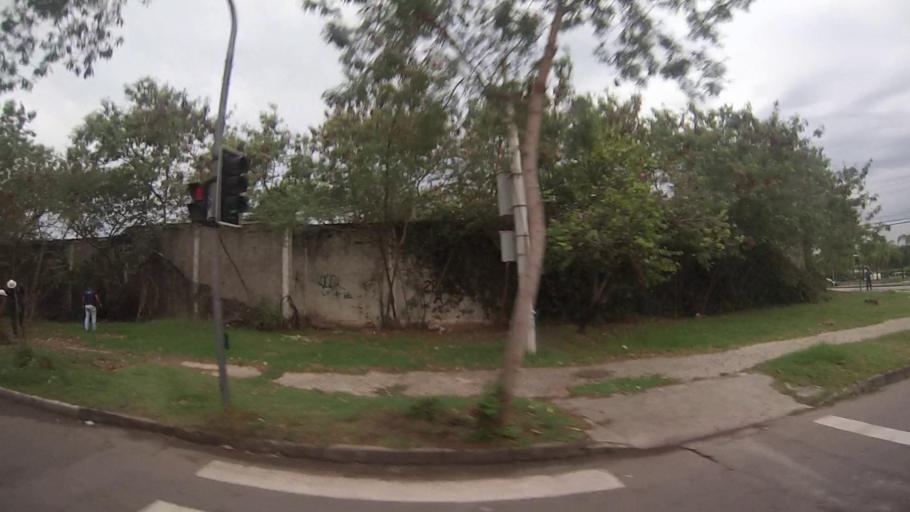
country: BR
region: Rio de Janeiro
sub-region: Rio De Janeiro
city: Rio de Janeiro
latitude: -22.9847
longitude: -43.3643
